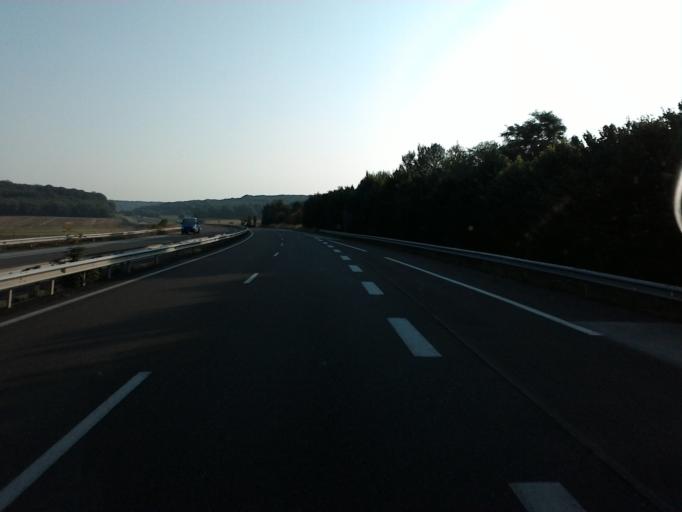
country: FR
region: Franche-Comte
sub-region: Departement de la Haute-Saone
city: Echenoz-la-Meline
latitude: 47.5586
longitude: 6.1360
